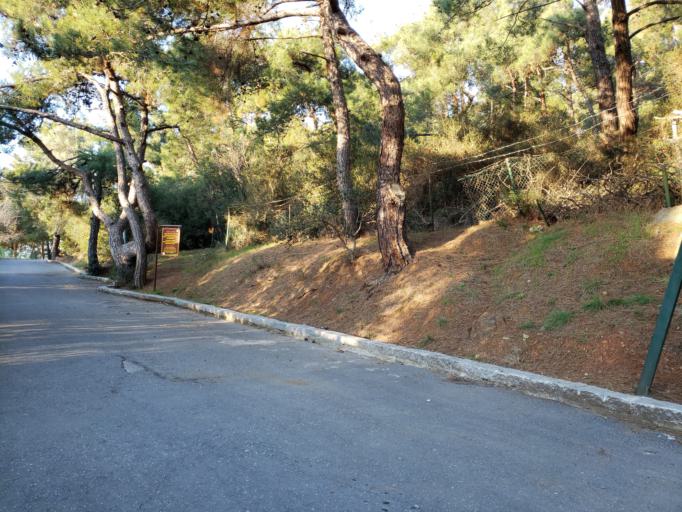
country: TR
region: Istanbul
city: Adalan
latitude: 40.8812
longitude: 29.0918
